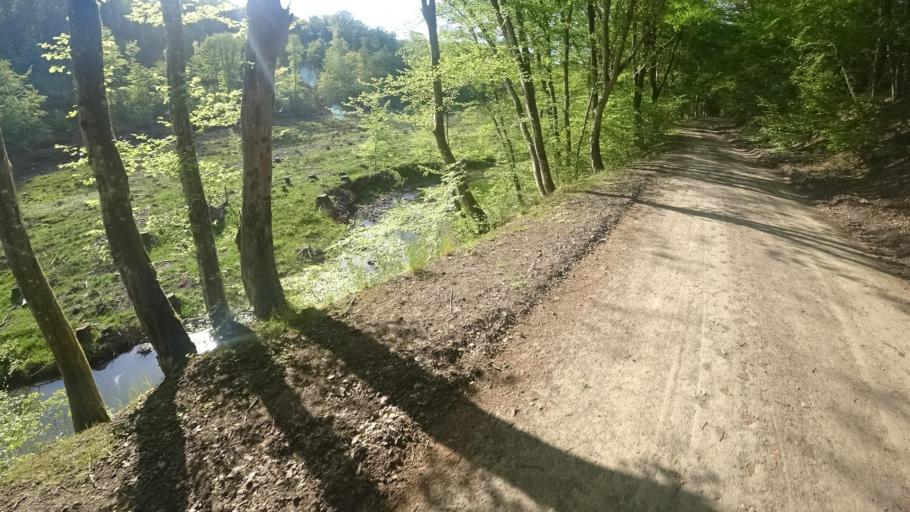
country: DE
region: Rheinland-Pfalz
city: Berg
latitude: 50.5369
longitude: 6.9723
